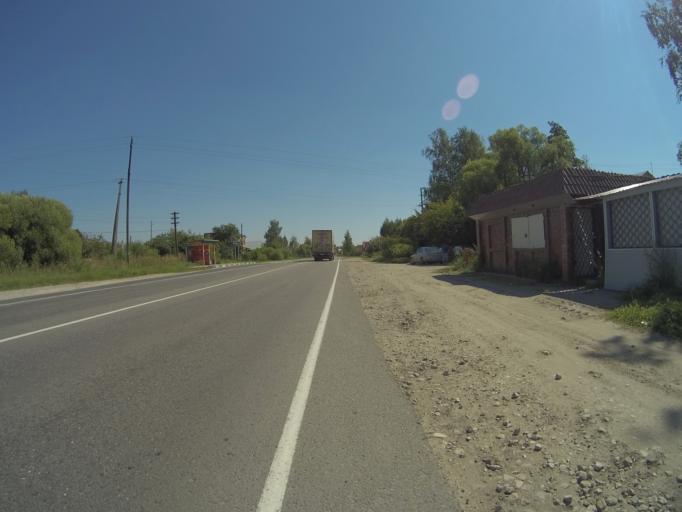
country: RU
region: Vladimir
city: Kommunar
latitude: 56.0462
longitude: 40.5375
